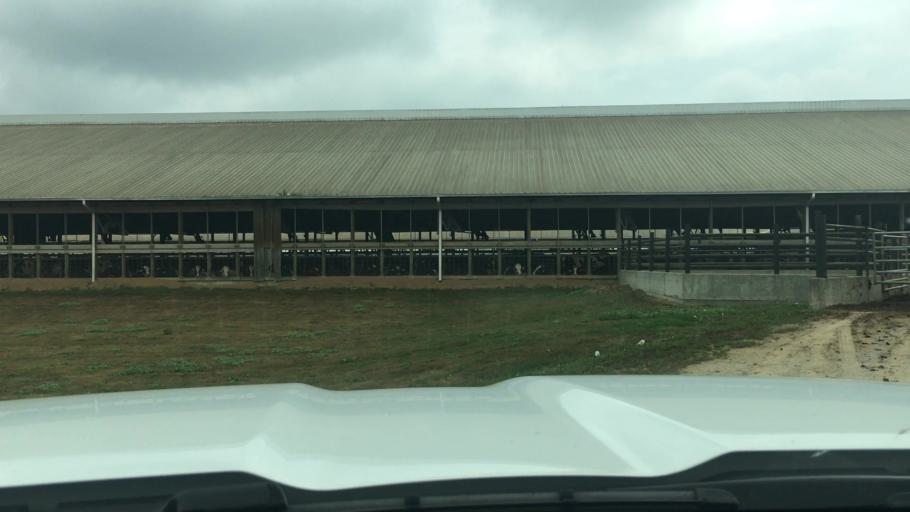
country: US
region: Michigan
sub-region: Sanilac County
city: Marlette
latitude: 43.3507
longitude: -82.9729
